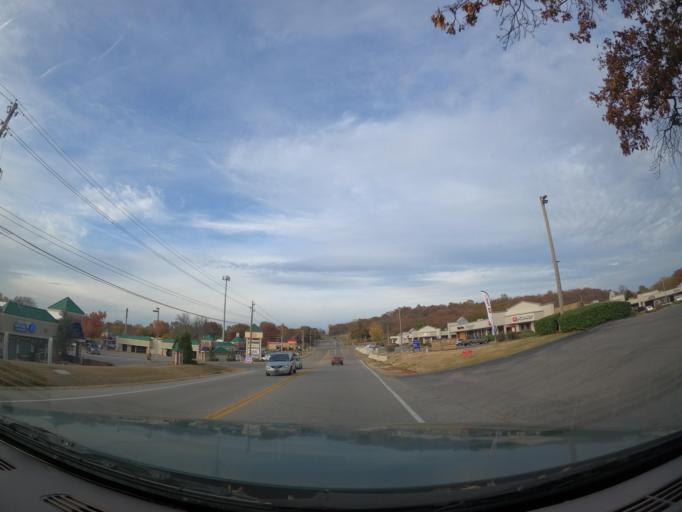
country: US
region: Oklahoma
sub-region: Tulsa County
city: Jenks
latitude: 36.0444
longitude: -95.9400
